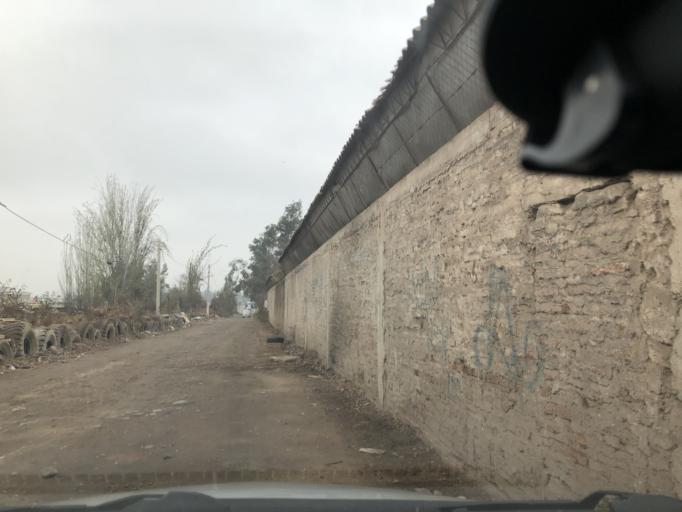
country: CL
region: Santiago Metropolitan
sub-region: Provincia de Cordillera
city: Puente Alto
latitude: -33.5976
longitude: -70.6035
